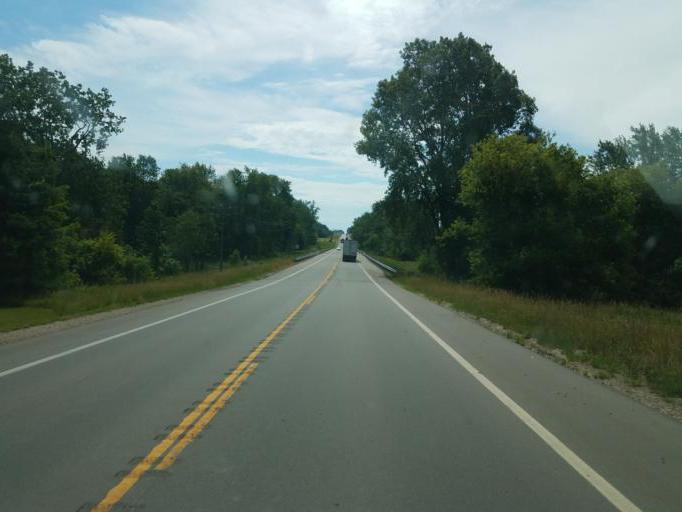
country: US
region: Michigan
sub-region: Eaton County
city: Charlotte
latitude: 42.6395
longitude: -84.8835
